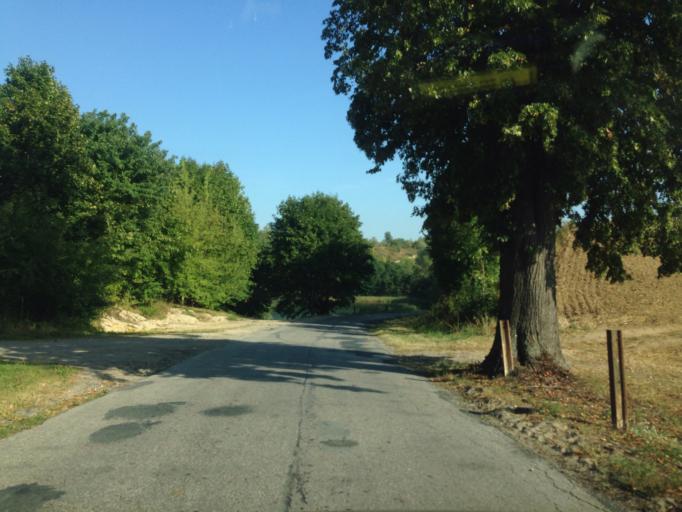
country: PL
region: Kujawsko-Pomorskie
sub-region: Powiat brodnicki
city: Brzozie
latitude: 53.3027
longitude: 19.6146
